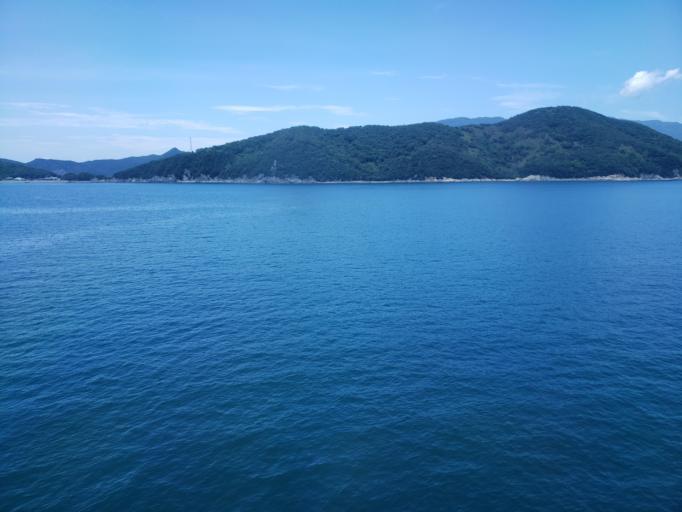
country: JP
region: Kagawa
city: Tonosho
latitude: 34.4404
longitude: 134.3002
